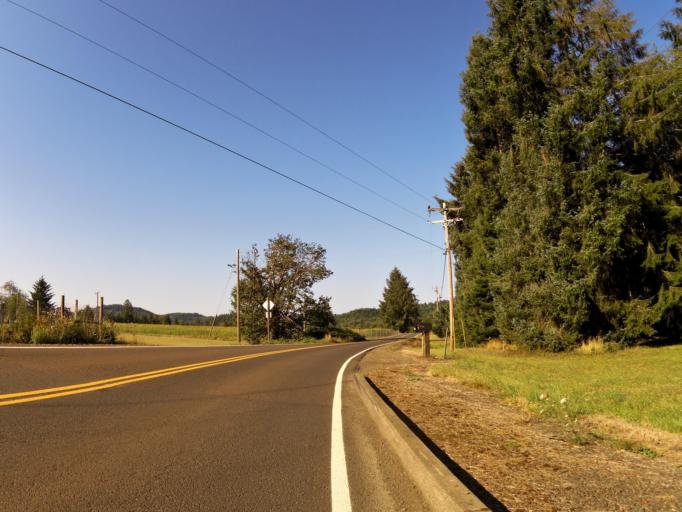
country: US
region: Oregon
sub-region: Tillamook County
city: Tillamook
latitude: 45.3856
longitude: -123.7961
